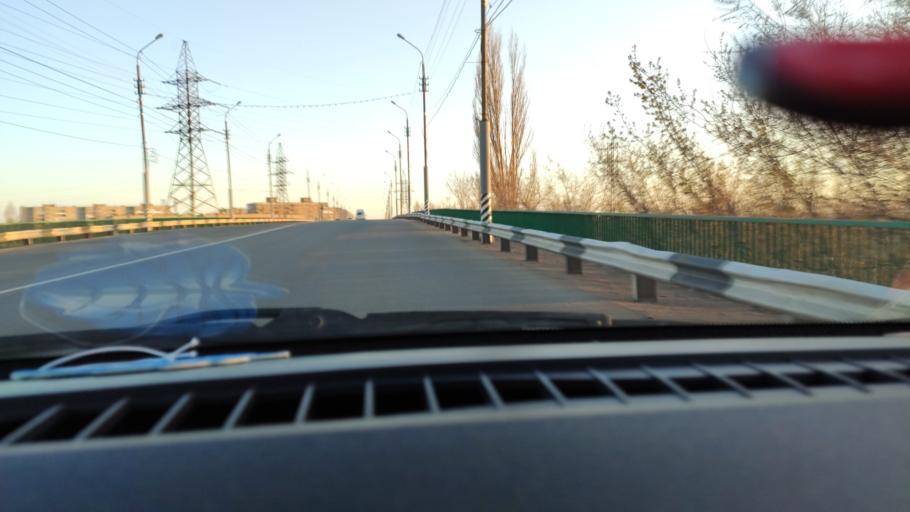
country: RU
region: Saratov
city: Privolzhskiy
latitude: 51.4150
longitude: 46.0441
